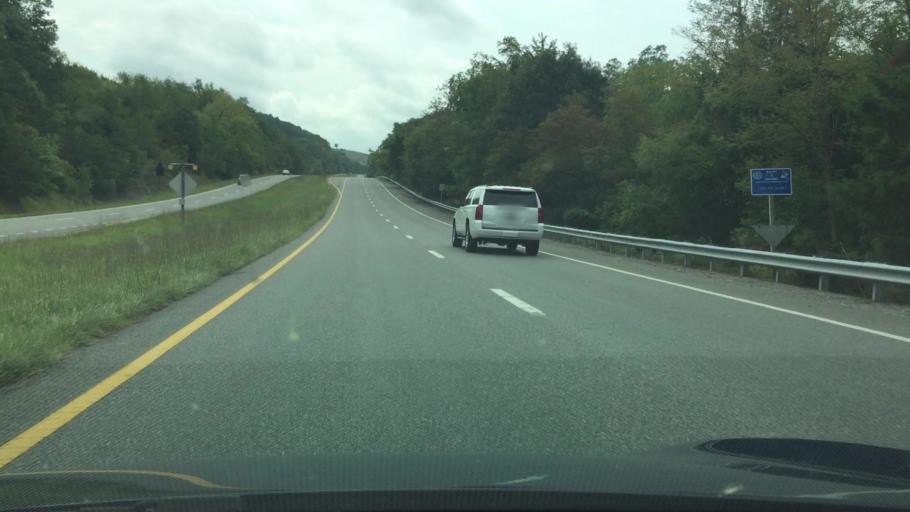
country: US
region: Virginia
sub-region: City of Radford
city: Radford
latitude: 37.1185
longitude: -80.5318
